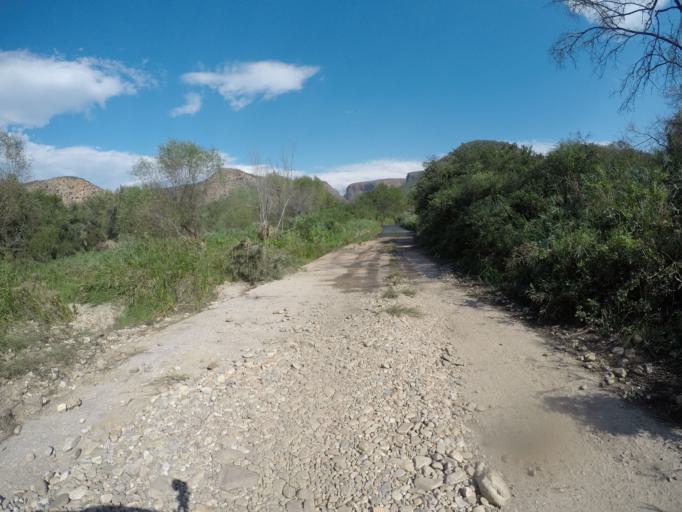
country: ZA
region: Eastern Cape
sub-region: Cacadu District Municipality
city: Kareedouw
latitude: -33.6657
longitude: 24.3864
